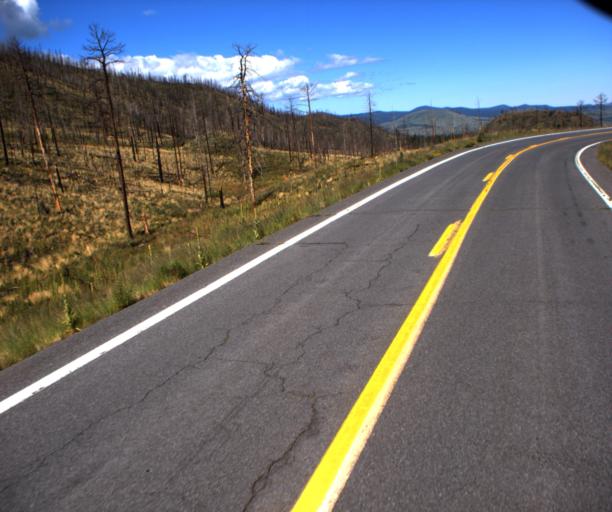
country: US
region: Arizona
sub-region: Apache County
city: Eagar
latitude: 34.0478
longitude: -109.3608
